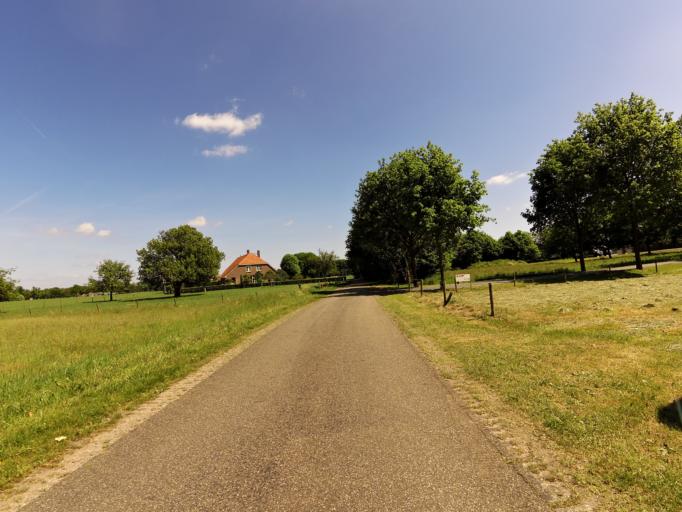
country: NL
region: Gelderland
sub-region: Gemeente Bronckhorst
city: Hengelo
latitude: 52.0889
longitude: 6.3076
